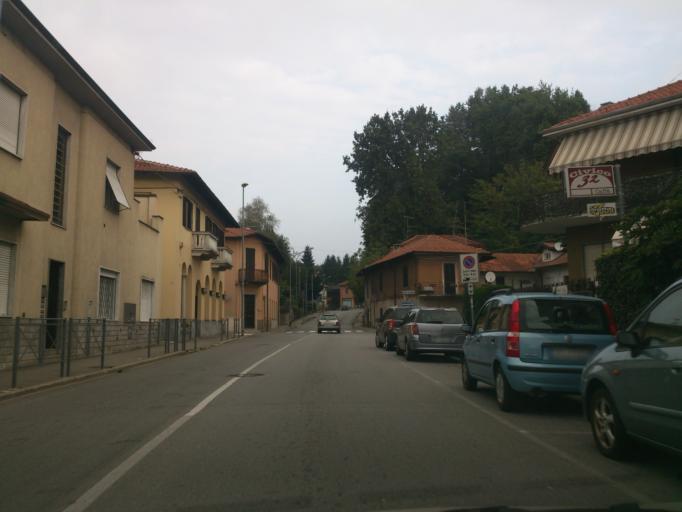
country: IT
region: Lombardy
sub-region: Provincia di Varese
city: Cassano Magnago
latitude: 45.6745
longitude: 8.8229
